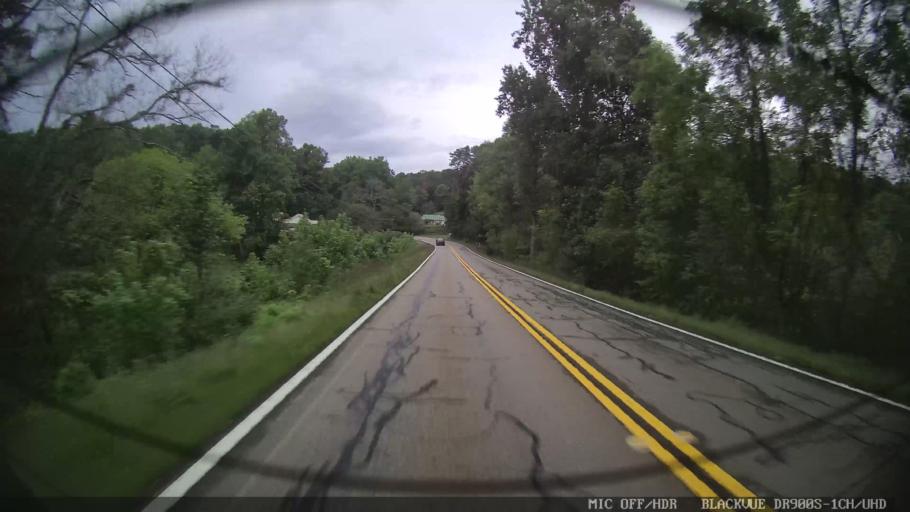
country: US
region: Georgia
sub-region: Gilmer County
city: Ellijay
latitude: 34.7369
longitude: -84.5172
